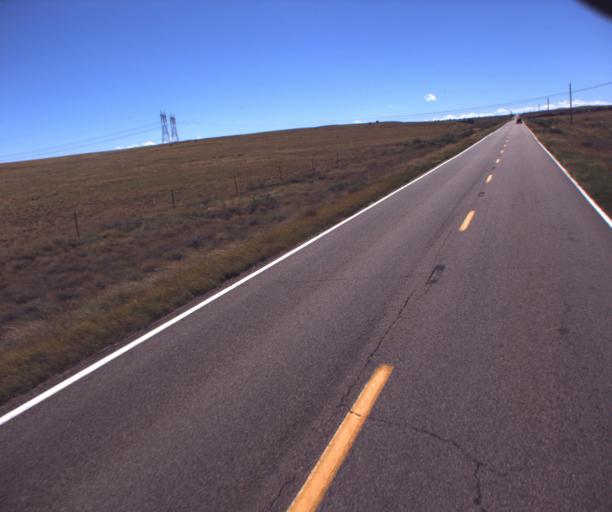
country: US
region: Arizona
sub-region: Apache County
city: Saint Johns
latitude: 34.5825
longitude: -109.3324
